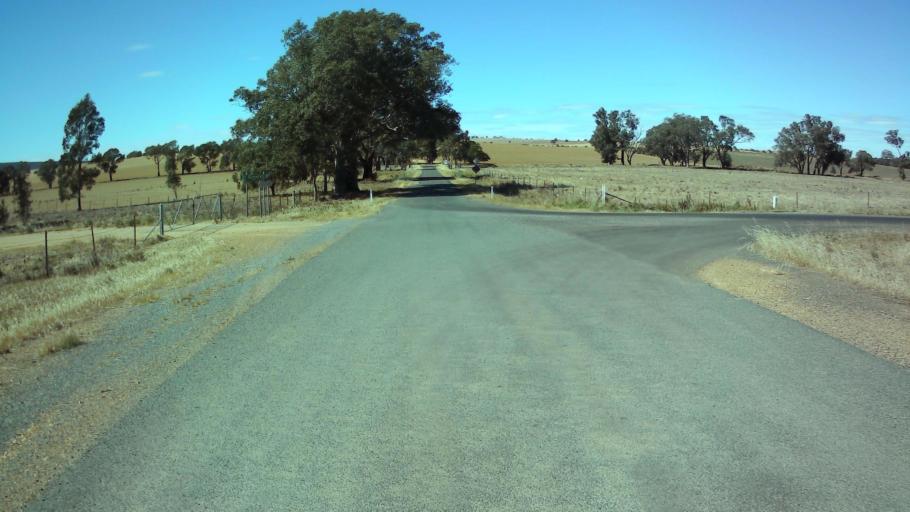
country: AU
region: New South Wales
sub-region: Weddin
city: Grenfell
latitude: -33.9980
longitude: 148.4101
